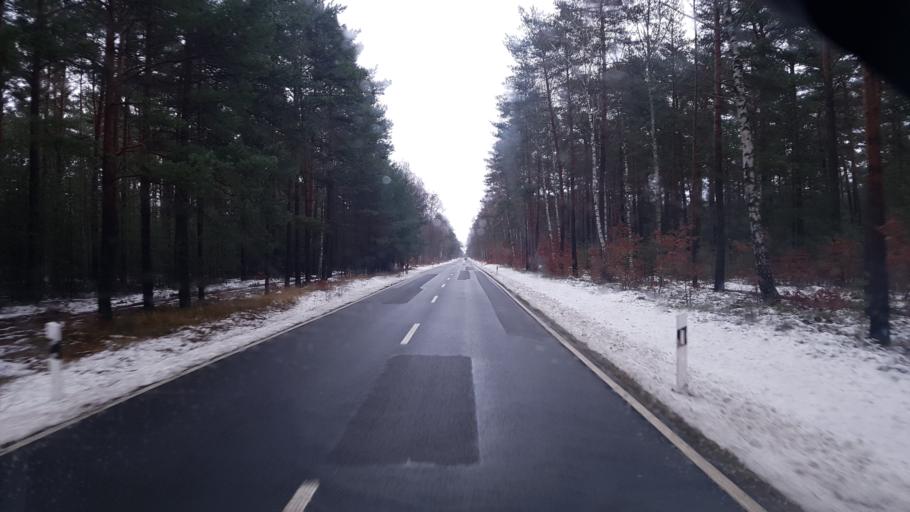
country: DE
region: Brandenburg
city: Tauer
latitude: 51.9804
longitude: 14.4774
